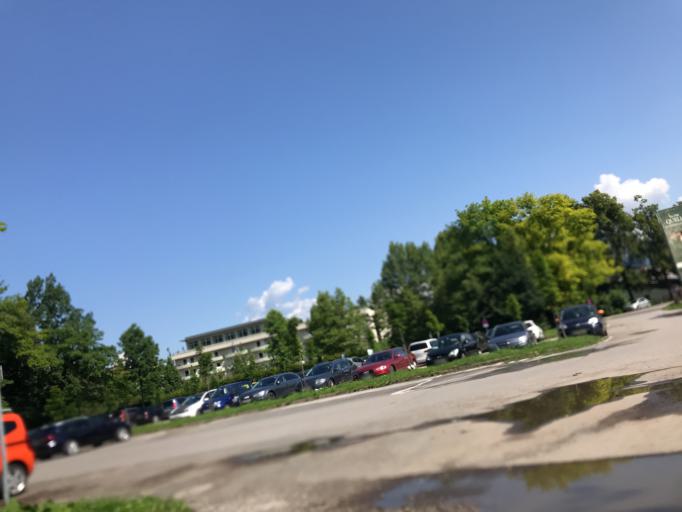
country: AT
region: Carinthia
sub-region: Villach Stadt
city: Villach
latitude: 46.5865
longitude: 13.8326
